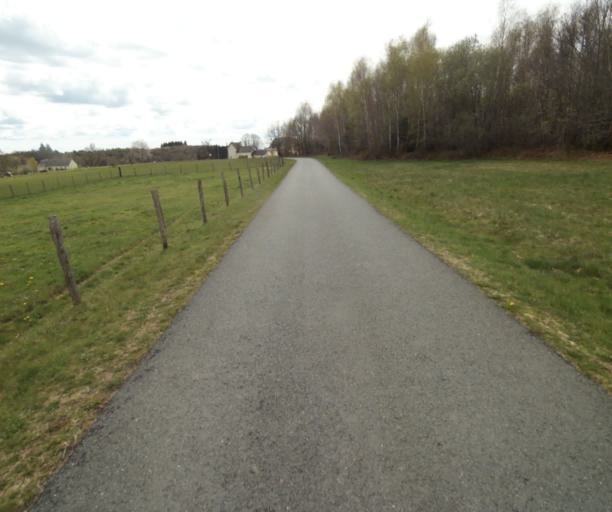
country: FR
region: Limousin
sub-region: Departement de la Correze
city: Laguenne
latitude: 45.2020
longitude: 1.8883
